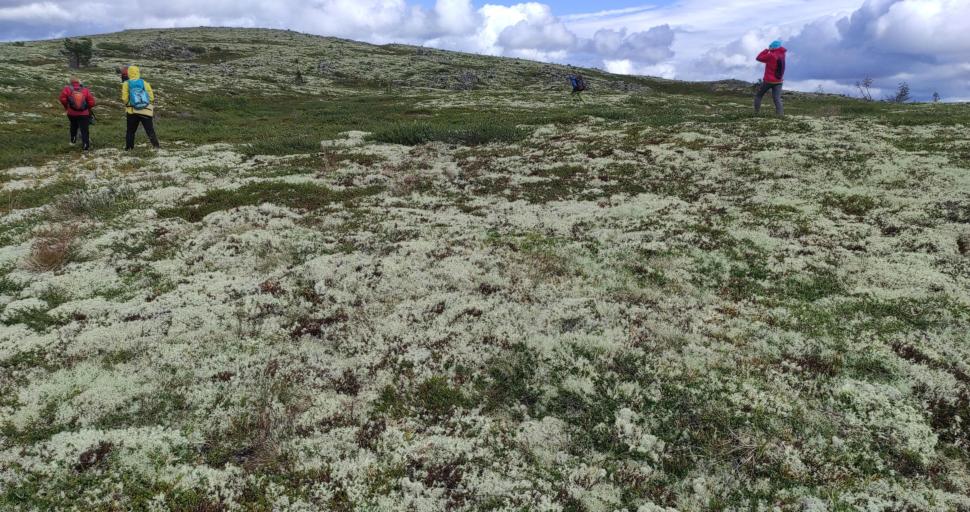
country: RU
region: Murmansk
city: Afrikanda
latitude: 67.0420
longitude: 32.9379
